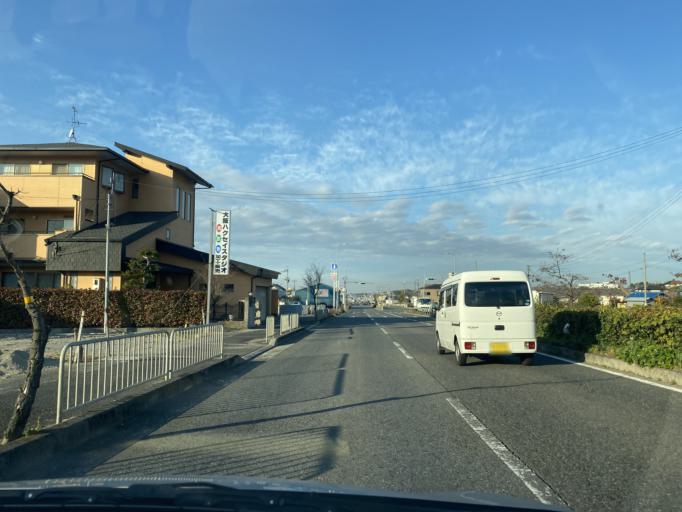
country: JP
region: Osaka
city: Izumi
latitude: 34.4277
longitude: 135.4401
